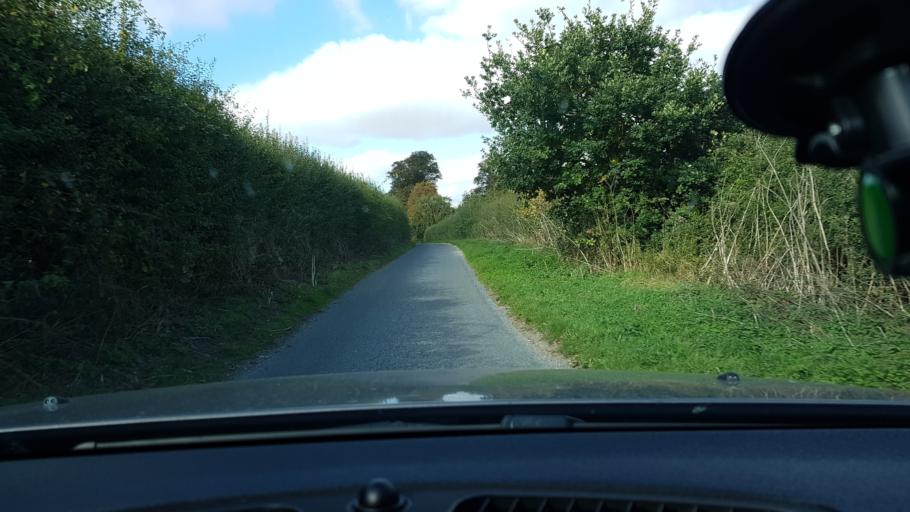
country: GB
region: England
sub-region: West Berkshire
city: Wickham
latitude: 51.4259
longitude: -1.4495
